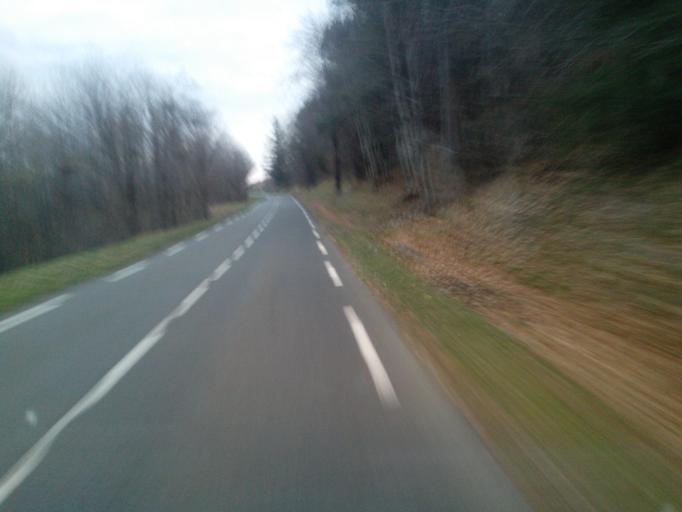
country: FR
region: Languedoc-Roussillon
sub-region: Departement du Gard
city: Valleraugue
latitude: 44.1829
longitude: 3.6798
